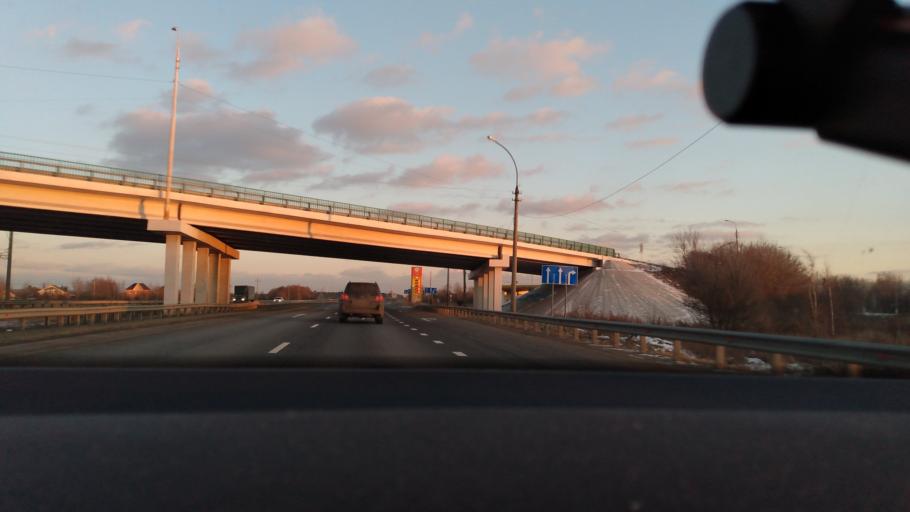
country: RU
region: Moskovskaya
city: Raduzhnyy
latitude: 55.1458
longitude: 38.7289
